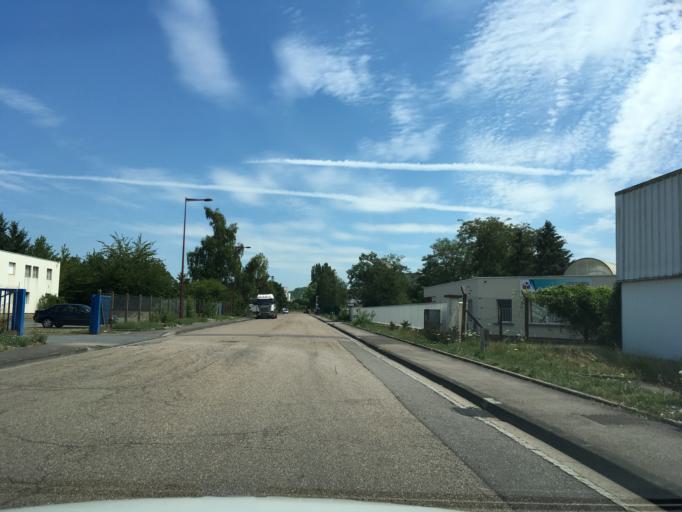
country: FR
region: Lorraine
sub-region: Departement de la Moselle
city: Metz
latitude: 49.1400
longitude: 6.1740
